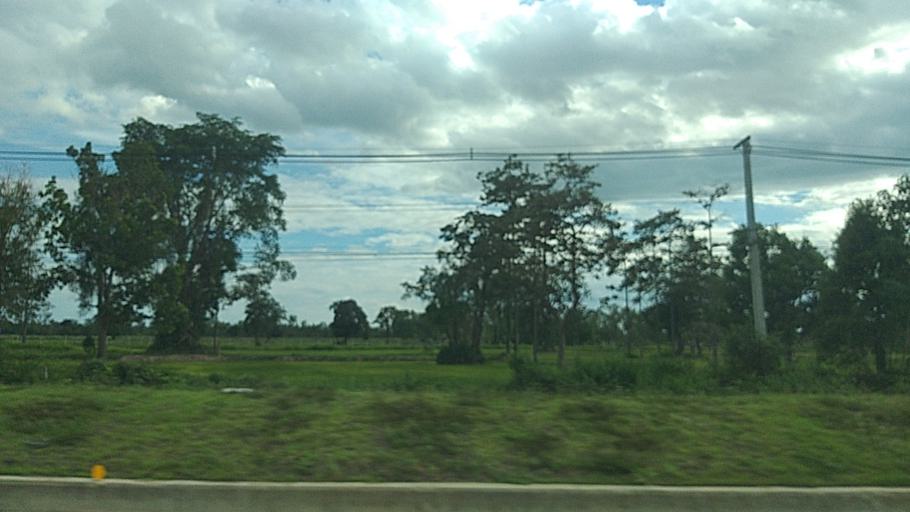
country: TH
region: Surin
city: Prasat
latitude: 14.5692
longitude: 103.4895
